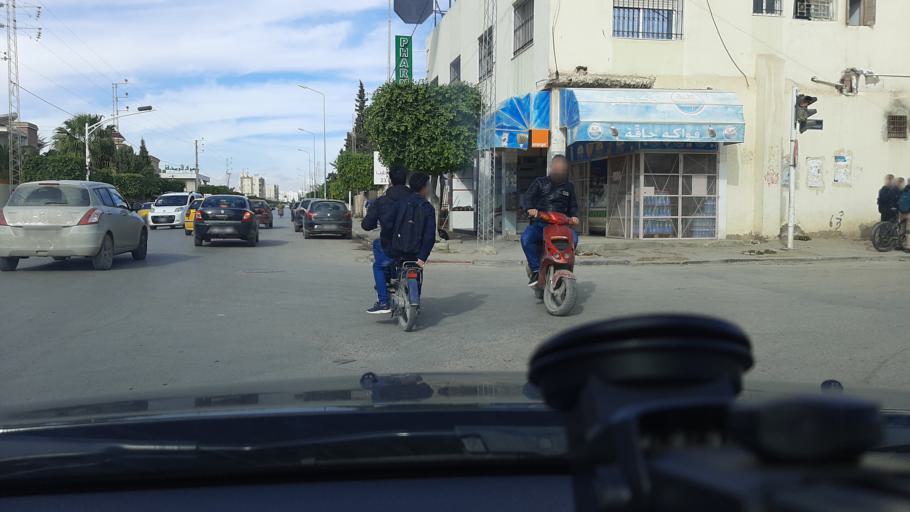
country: TN
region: Safaqis
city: Sfax
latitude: 34.7703
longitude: 10.7330
